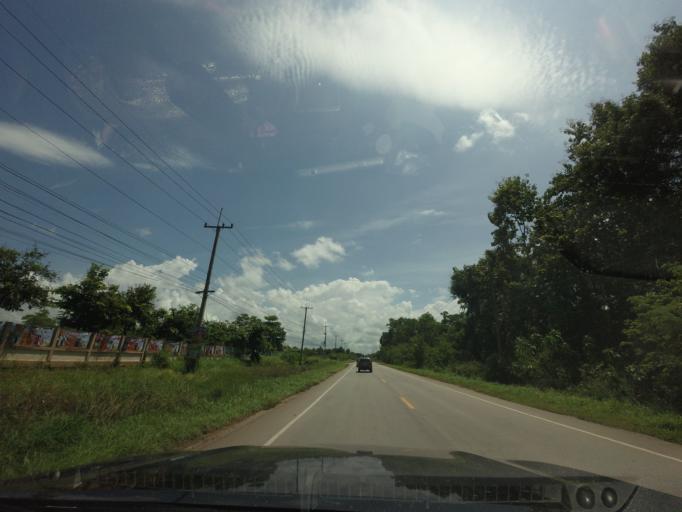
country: TH
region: Changwat Udon Thani
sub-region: Amphoe Ban Phue
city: Ban Phue
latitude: 17.7021
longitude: 102.4382
